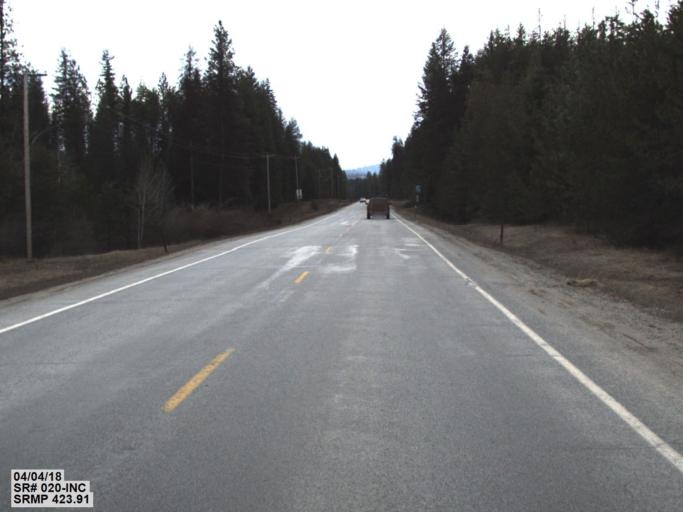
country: US
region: Washington
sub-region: Pend Oreille County
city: Newport
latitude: 48.2730
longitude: -117.2624
